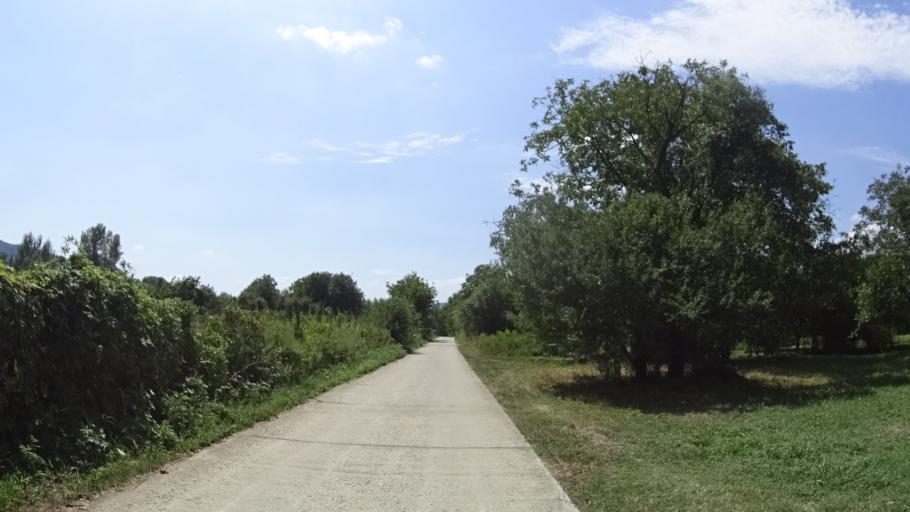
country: HU
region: Pest
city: Kismaros
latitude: 47.8162
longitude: 18.9827
